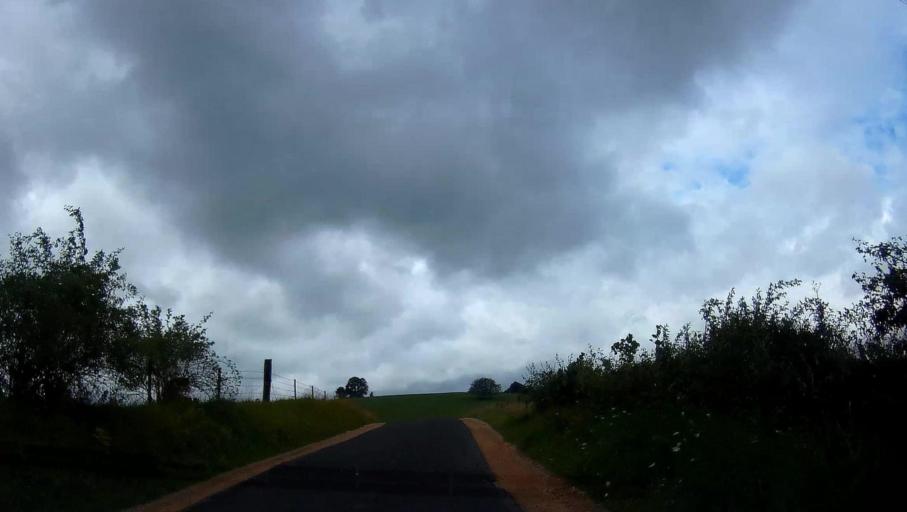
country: FR
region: Champagne-Ardenne
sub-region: Departement des Ardennes
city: Rimogne
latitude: 49.7590
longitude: 4.5224
